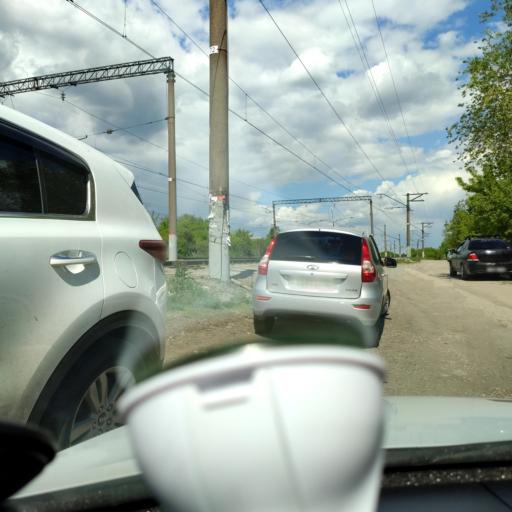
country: RU
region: Samara
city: Petra-Dubrava
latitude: 53.2712
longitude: 50.3176
